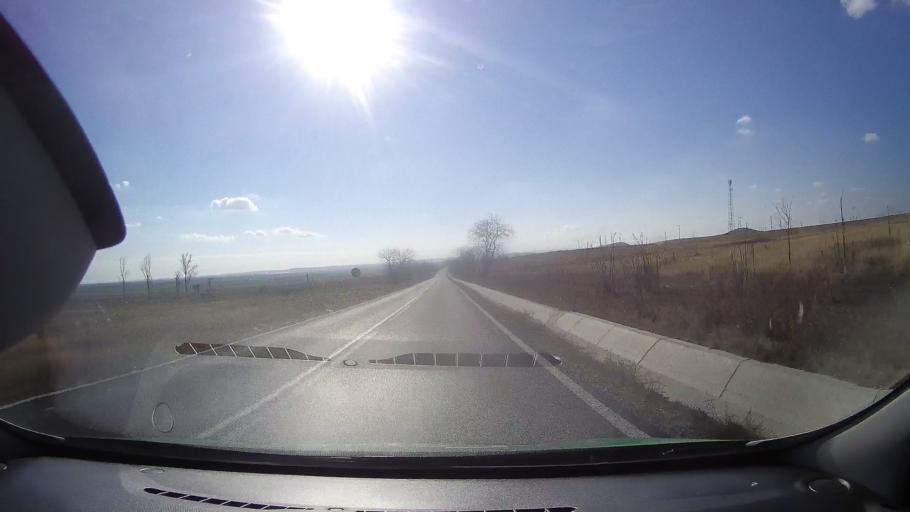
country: RO
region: Tulcea
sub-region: Comuna Ceamurlia de Jos
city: Ceamurlia de Jos
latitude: 44.8119
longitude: 28.6915
